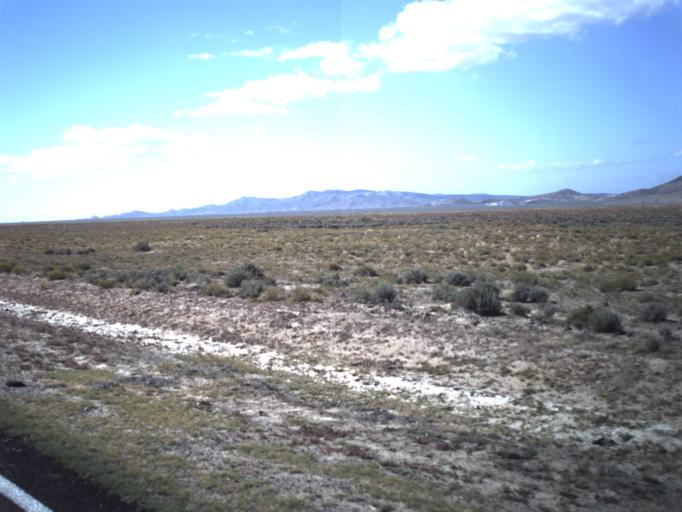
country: US
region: Utah
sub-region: Beaver County
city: Milford
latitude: 38.4769
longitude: -112.9913
